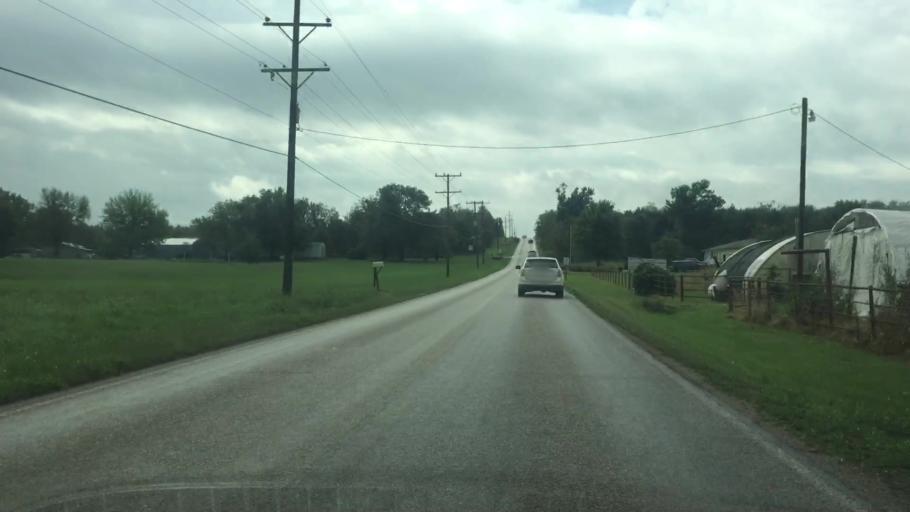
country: US
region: Kansas
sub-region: Allen County
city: Humboldt
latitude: 37.8658
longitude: -95.4369
